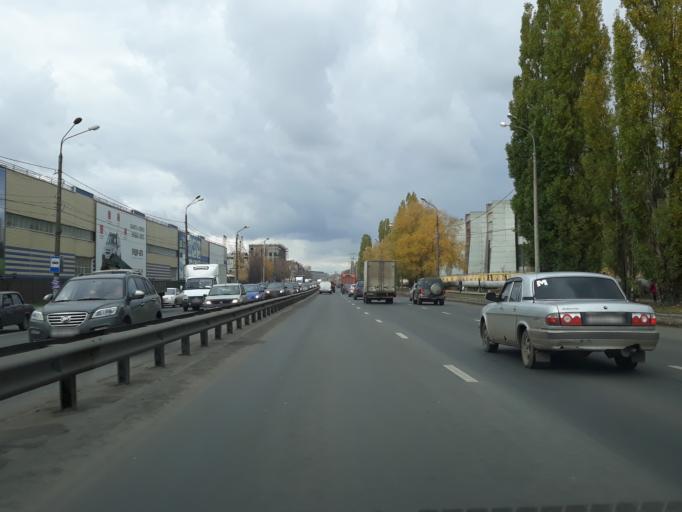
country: RU
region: Nizjnij Novgorod
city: Nizhniy Novgorod
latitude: 56.2615
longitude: 43.9267
